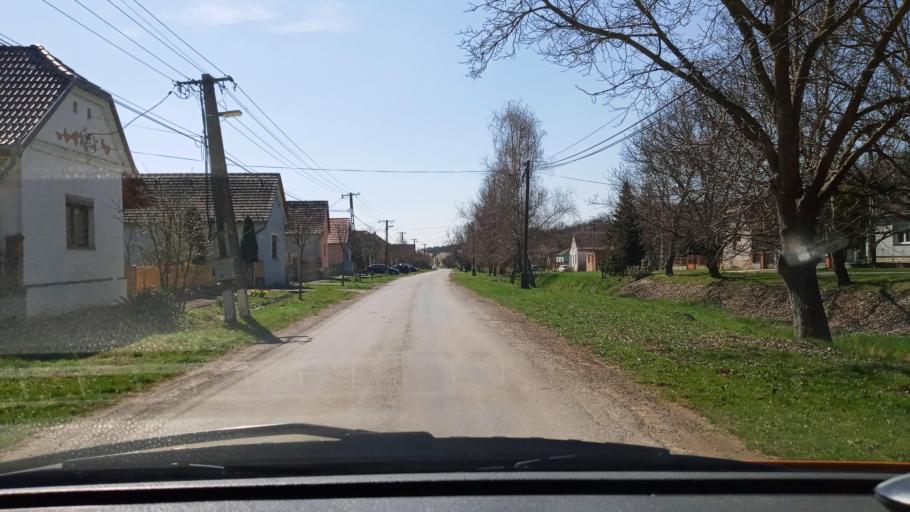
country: HU
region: Baranya
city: Pecsvarad
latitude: 46.0670
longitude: 18.4492
